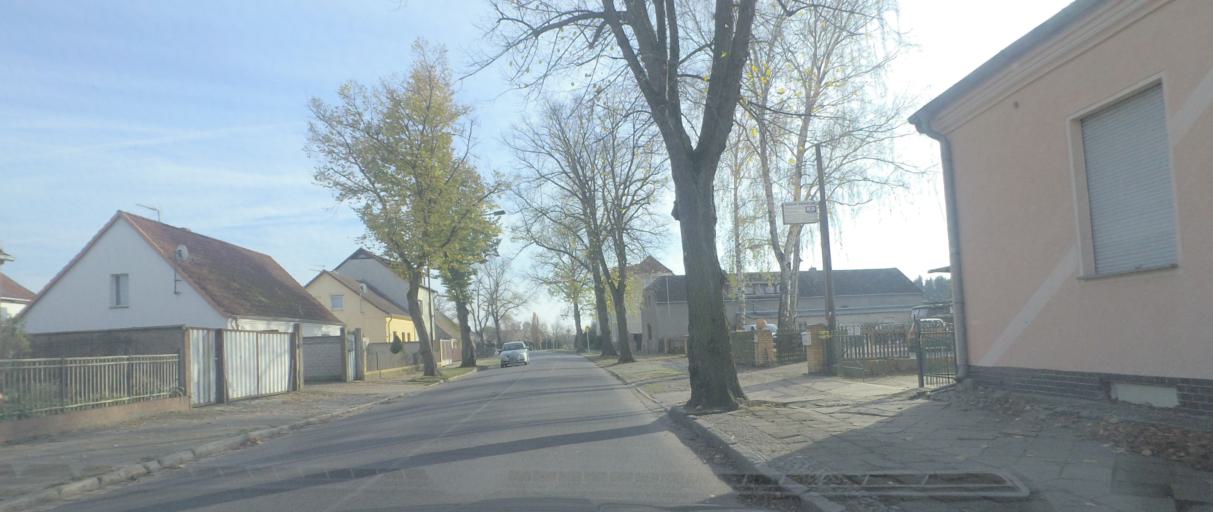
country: DE
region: Brandenburg
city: Sperenberg
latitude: 52.1369
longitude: 13.3660
